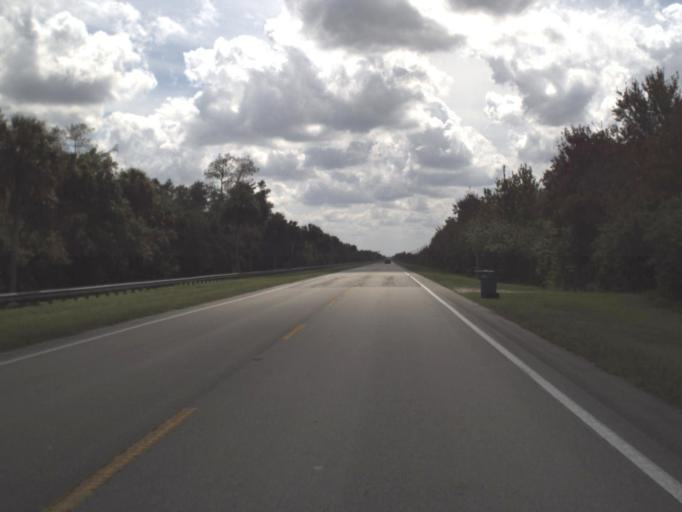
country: US
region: Florida
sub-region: Collier County
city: Orangetree
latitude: 26.1108
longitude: -81.3448
